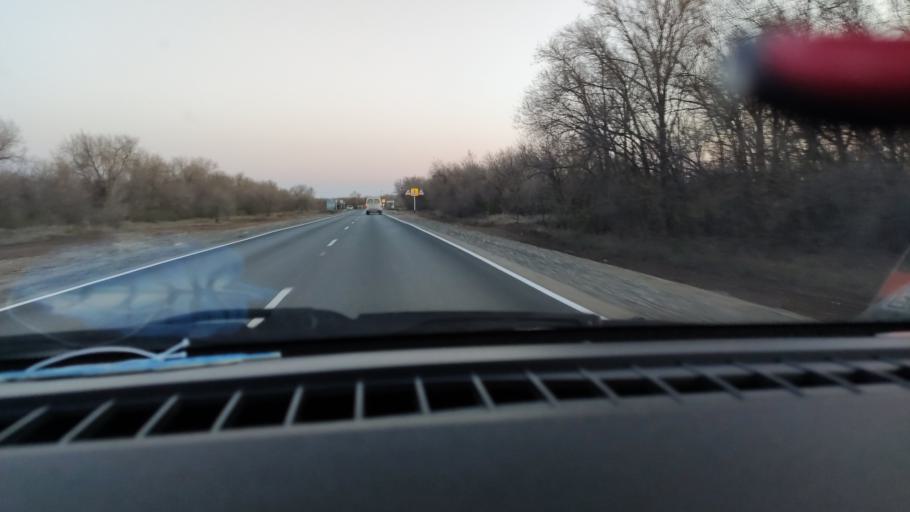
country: RU
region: Saratov
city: Krasnoarmeysk
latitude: 51.1201
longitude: 45.9561
